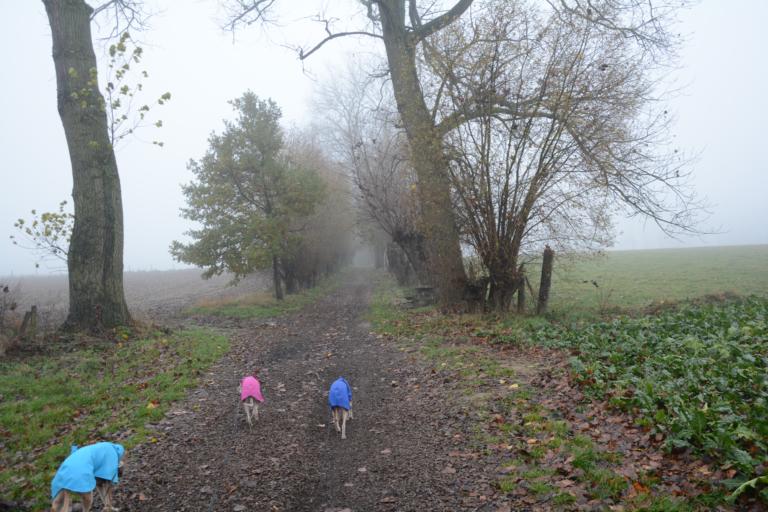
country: BE
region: Flanders
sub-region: Provincie Vlaams-Brabant
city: Wemmel
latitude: 50.9005
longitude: 4.2645
